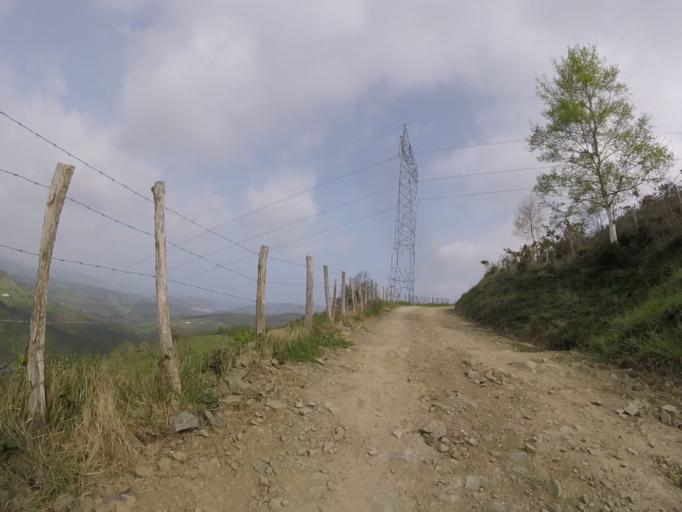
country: ES
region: Basque Country
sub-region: Provincia de Guipuzcoa
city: Zizurkil
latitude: 43.2321
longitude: -2.0883
